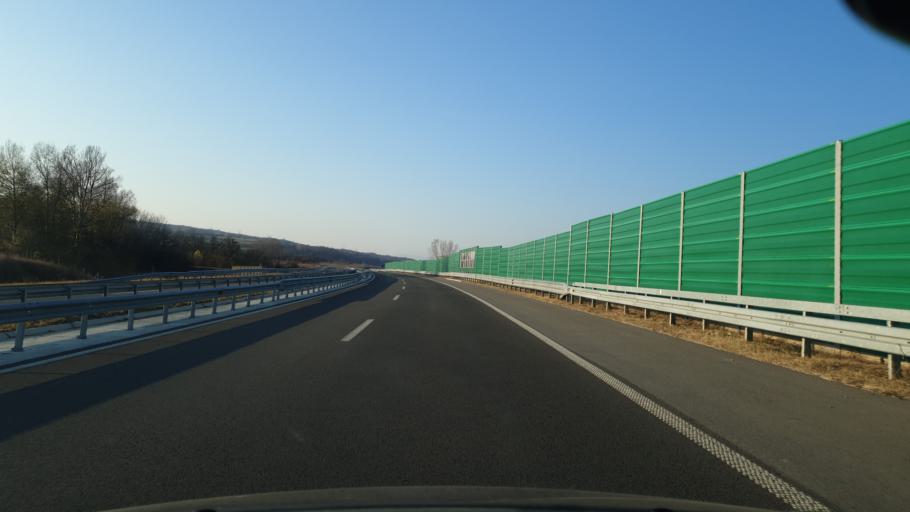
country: RS
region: Central Serbia
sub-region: Pirotski Okrug
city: Dimitrovgrad
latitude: 43.0345
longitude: 22.7190
